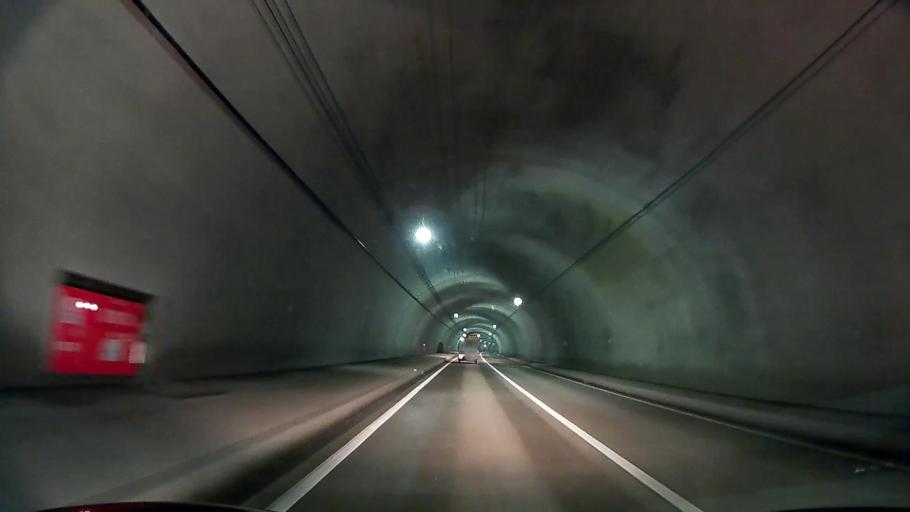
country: JP
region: Gunma
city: Nakanojomachi
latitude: 36.5334
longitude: 138.7108
